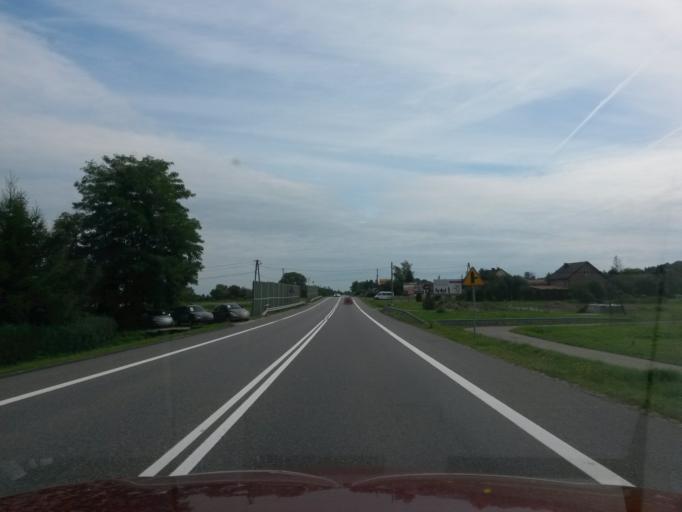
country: PL
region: Lesser Poland Voivodeship
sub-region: Powiat bochenski
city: Jodlowka
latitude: 49.9744
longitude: 20.5483
